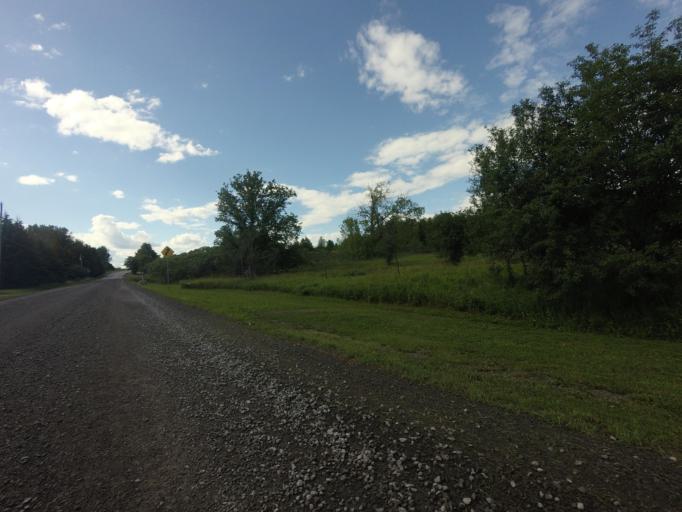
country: CA
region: Ontario
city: Arnprior
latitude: 45.3373
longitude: -76.1898
